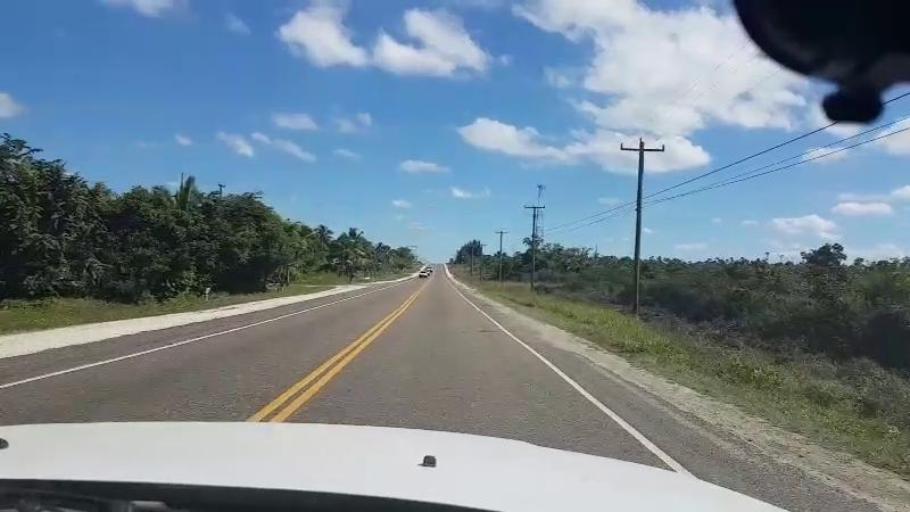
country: BZ
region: Cayo
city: Belmopan
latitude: 17.2770
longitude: -88.6649
